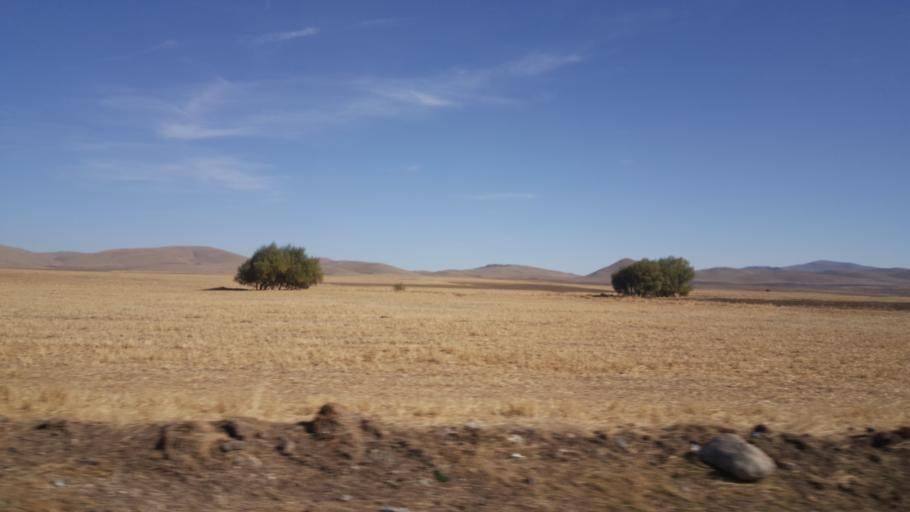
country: TR
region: Ankara
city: Yenice
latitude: 39.2817
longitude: 32.7554
